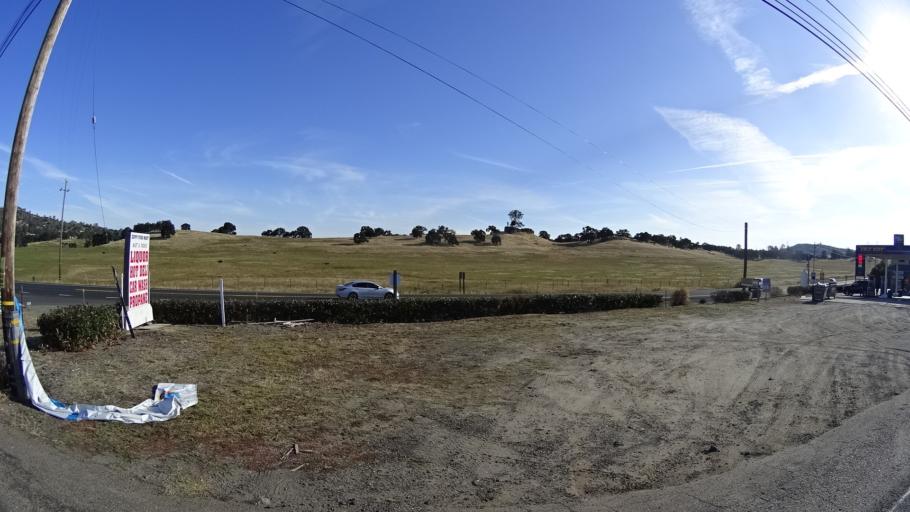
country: US
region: California
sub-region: Calaveras County
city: Valley Springs
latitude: 38.1932
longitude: -120.8204
